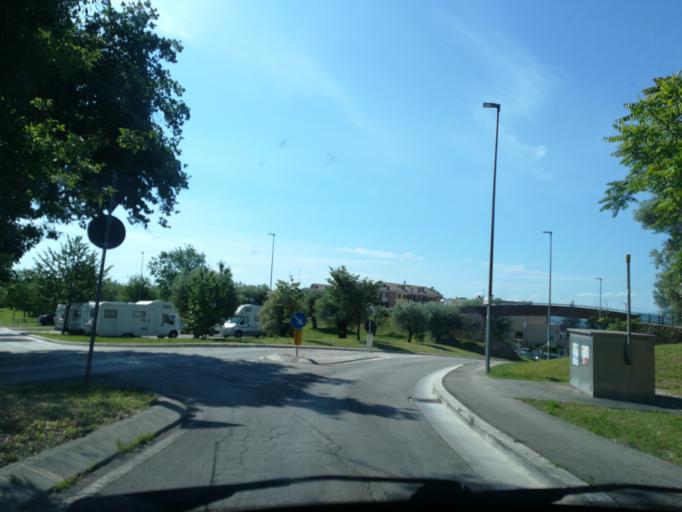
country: IT
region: The Marches
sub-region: Provincia di Macerata
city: Macerata
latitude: 43.2928
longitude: 13.4722
